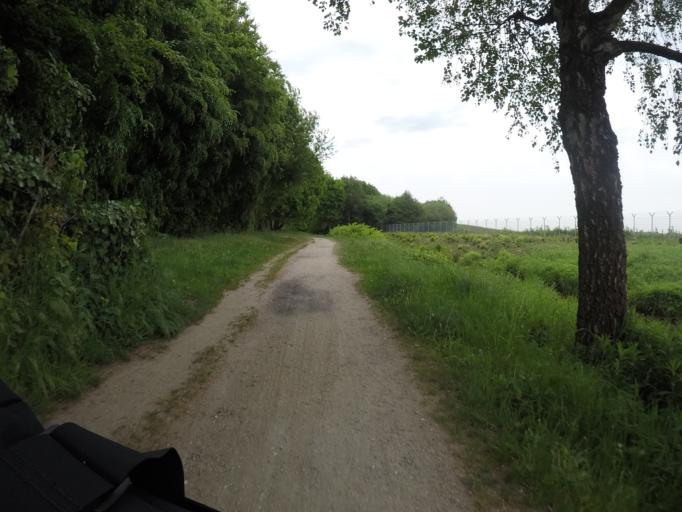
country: DE
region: Hamburg
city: Winterhude
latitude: 53.6281
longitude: 9.9787
